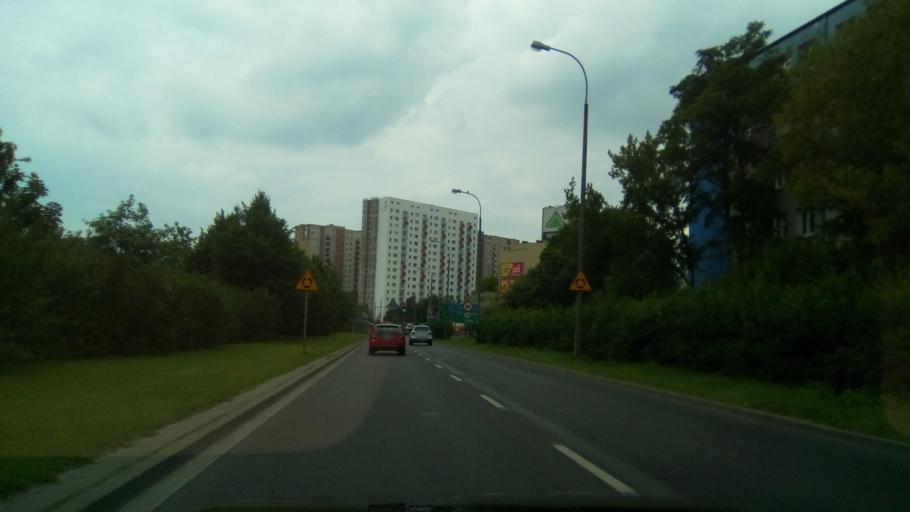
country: PL
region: Greater Poland Voivodeship
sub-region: Poznan
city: Poznan
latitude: 52.4341
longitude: 16.9413
